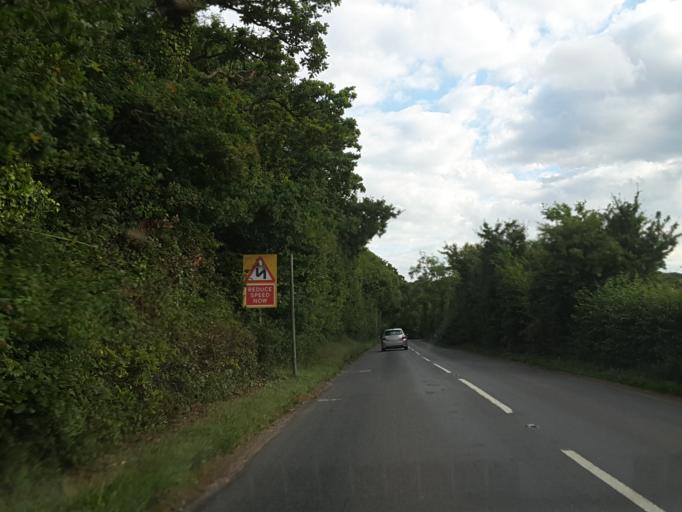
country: GB
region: England
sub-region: Isle of Wight
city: Newchurch
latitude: 50.6953
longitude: -1.2408
